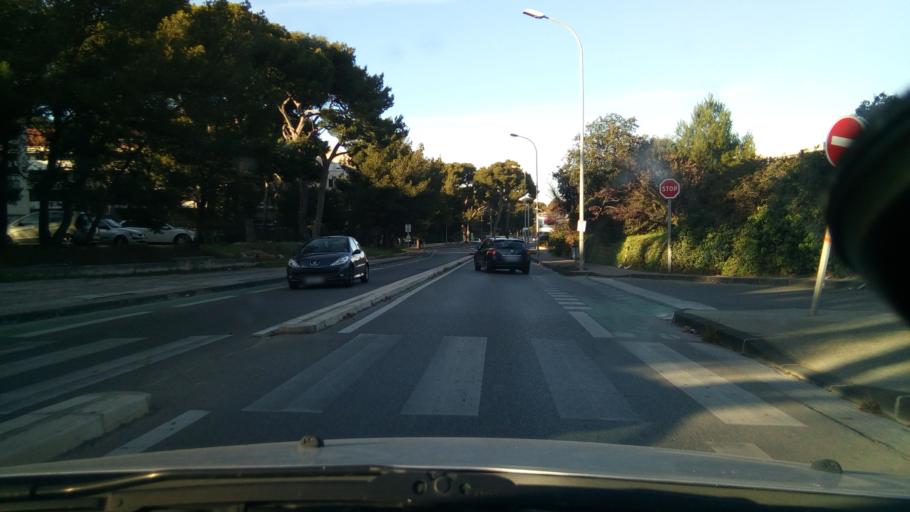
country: FR
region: Provence-Alpes-Cote d'Azur
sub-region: Departement des Bouches-du-Rhone
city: Marseille 09
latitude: 43.2332
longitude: 5.3999
